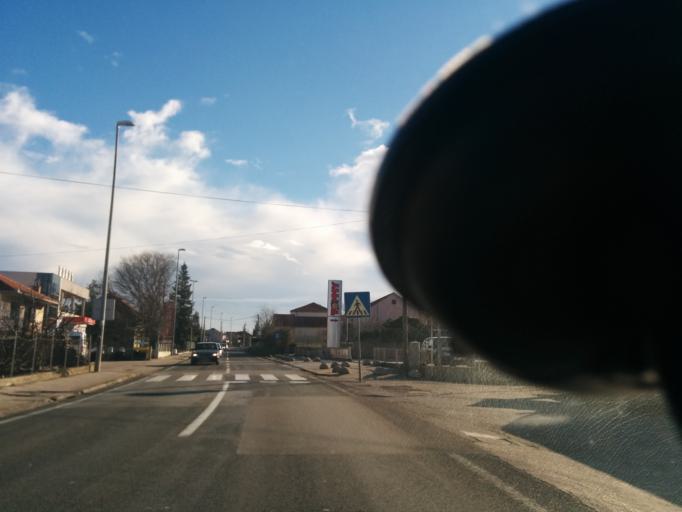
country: HR
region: Splitsko-Dalmatinska
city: Brnaze
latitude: 43.6907
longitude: 16.6459
